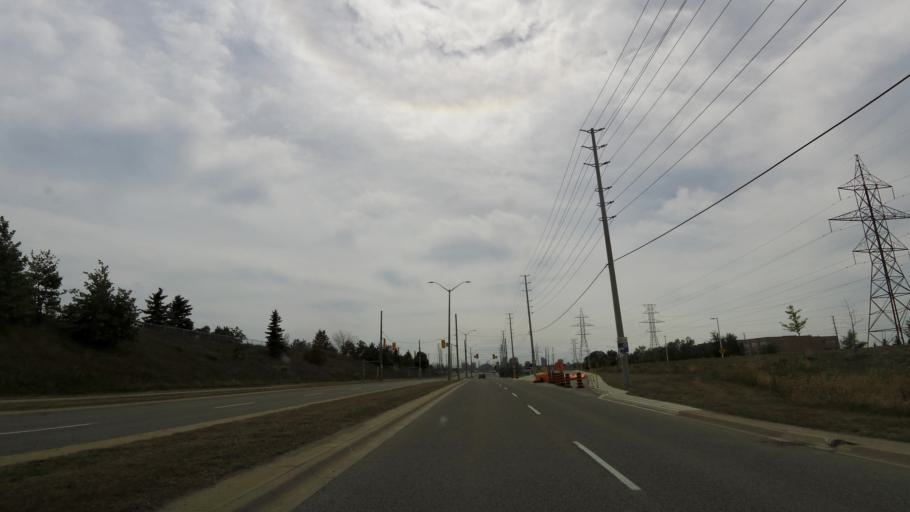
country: CA
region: Ontario
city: Etobicoke
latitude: 43.6331
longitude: -79.6103
